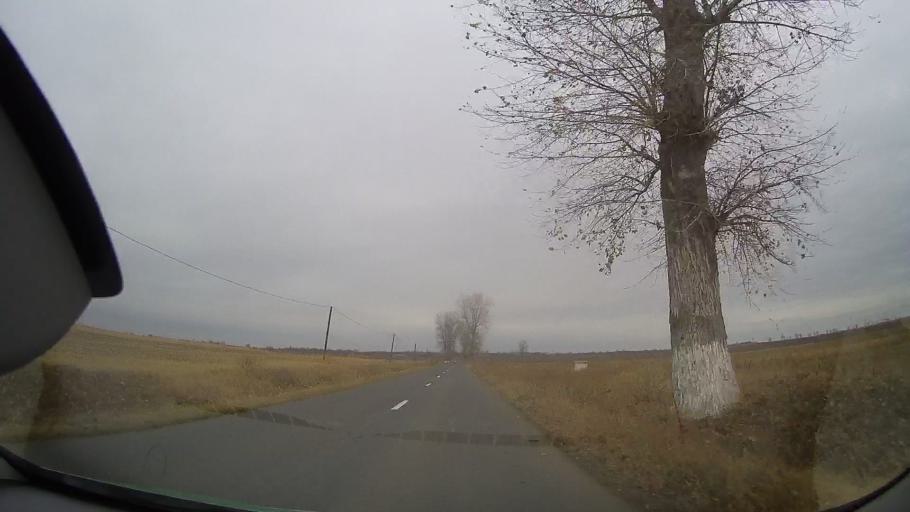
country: RO
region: Braila
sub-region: Comuna Budesti
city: Tataru
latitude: 44.8371
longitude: 27.4166
